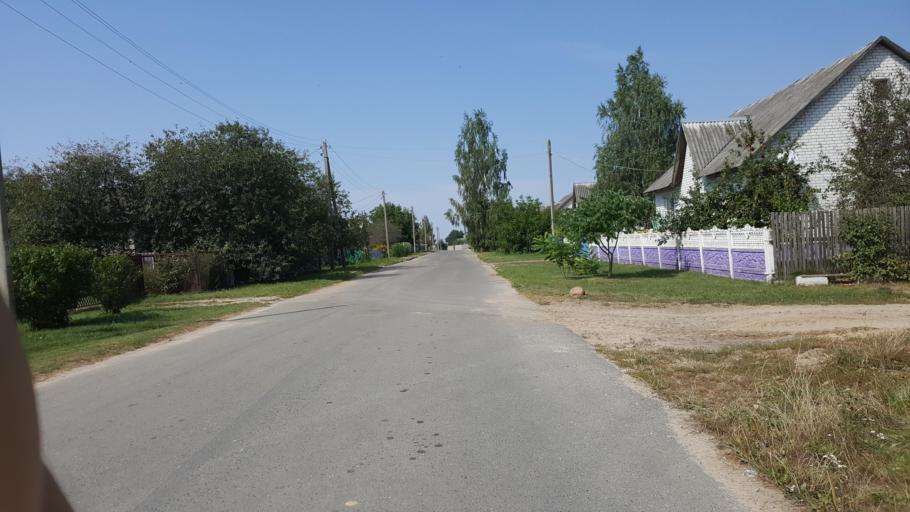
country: PL
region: Podlasie
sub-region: Powiat hajnowski
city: Czeremcha
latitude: 52.4982
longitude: 23.5741
